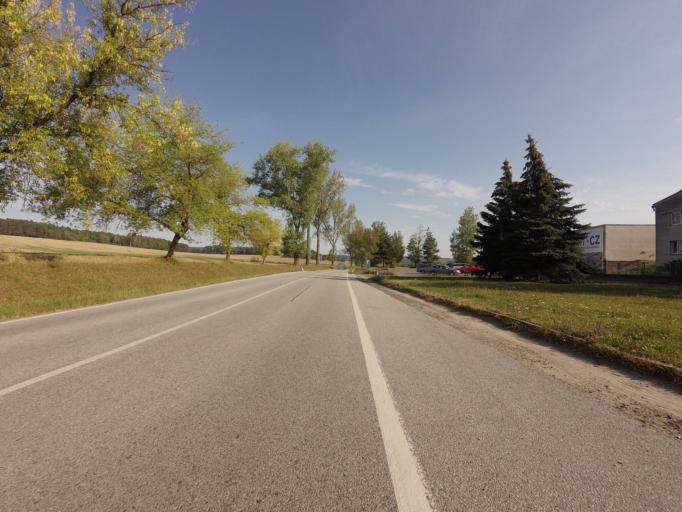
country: CZ
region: Jihocesky
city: Tyn nad Vltavou
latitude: 49.2329
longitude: 14.4214
